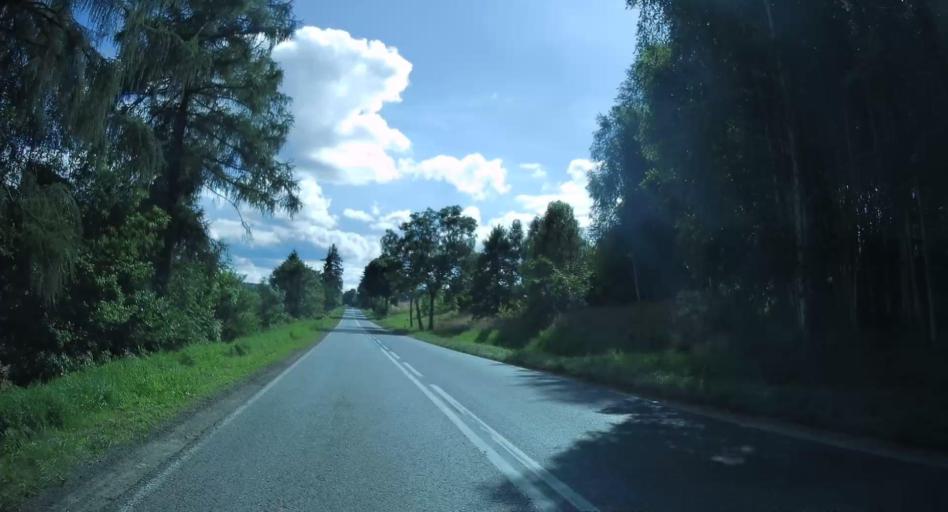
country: PL
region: Swietokrzyskie
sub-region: Powiat kielecki
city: Nowa Slupia
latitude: 50.8302
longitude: 21.0813
